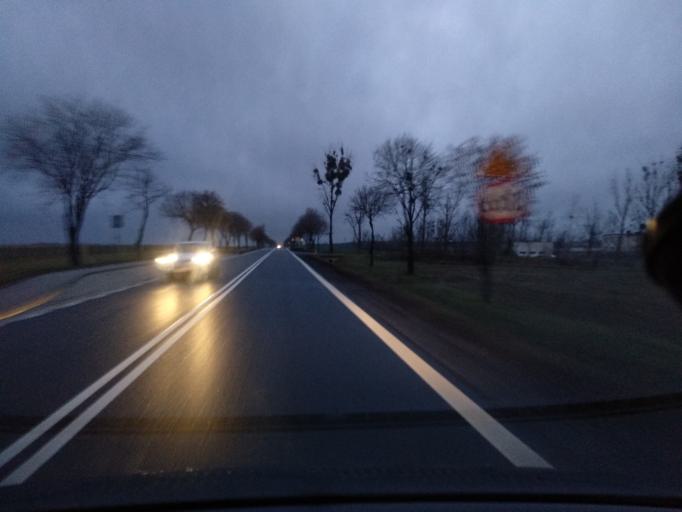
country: PL
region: Lower Silesian Voivodeship
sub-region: Powiat sredzki
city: Sroda Slaska
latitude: 51.1654
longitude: 16.5667
